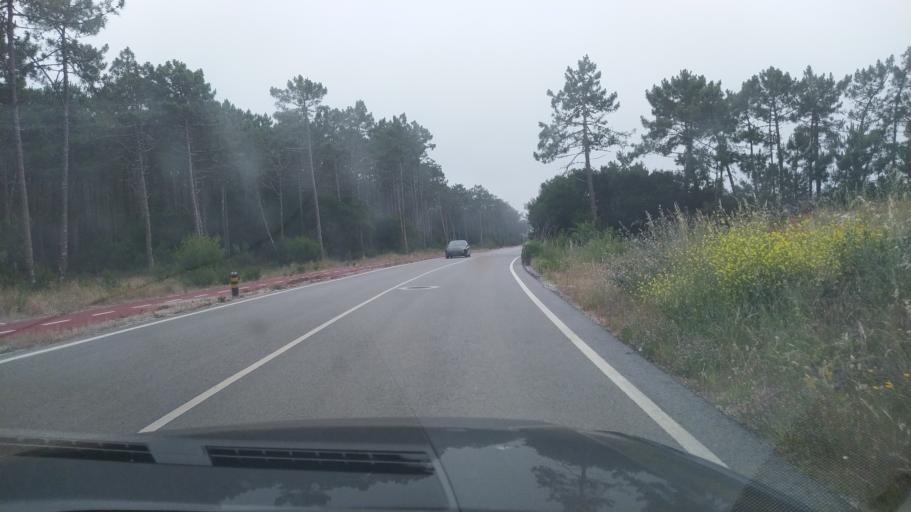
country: PT
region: Aveiro
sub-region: Ilhavo
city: Gafanha da Encarnacao
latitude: 40.5731
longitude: -8.7355
